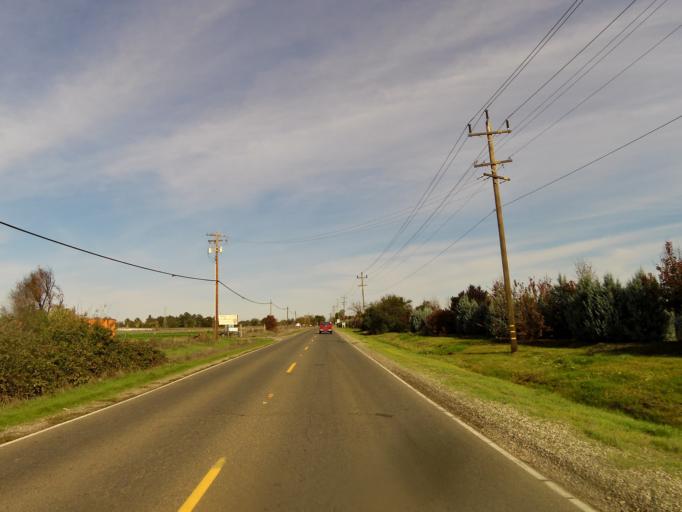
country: US
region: California
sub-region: Sacramento County
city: Wilton
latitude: 38.4161
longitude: -121.3173
